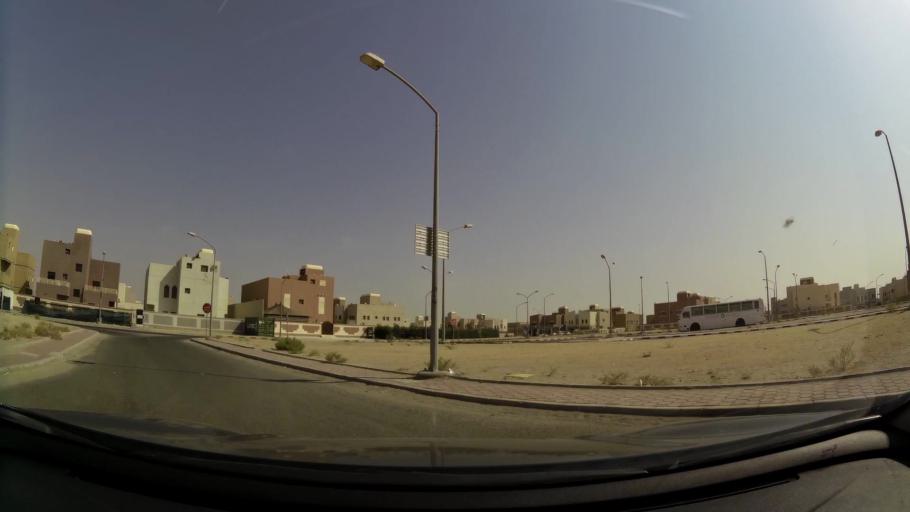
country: KW
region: Al Ahmadi
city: Al Wafrah
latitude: 28.8028
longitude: 48.0566
